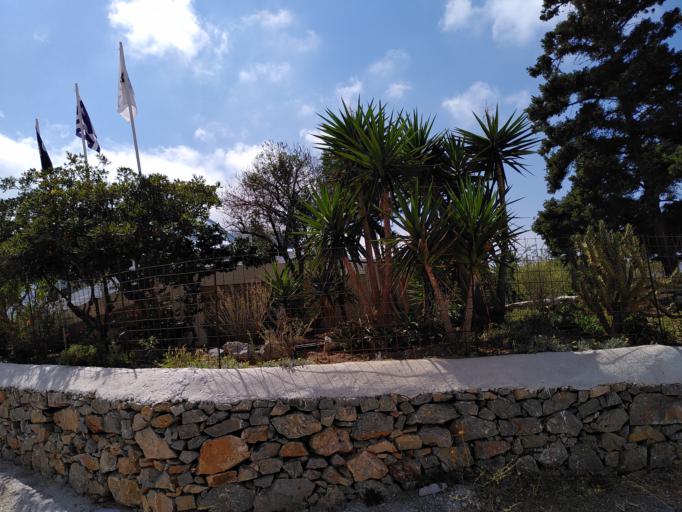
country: GR
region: South Aegean
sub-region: Nomos Kykladon
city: Amorgos
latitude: 36.9094
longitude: 25.9736
